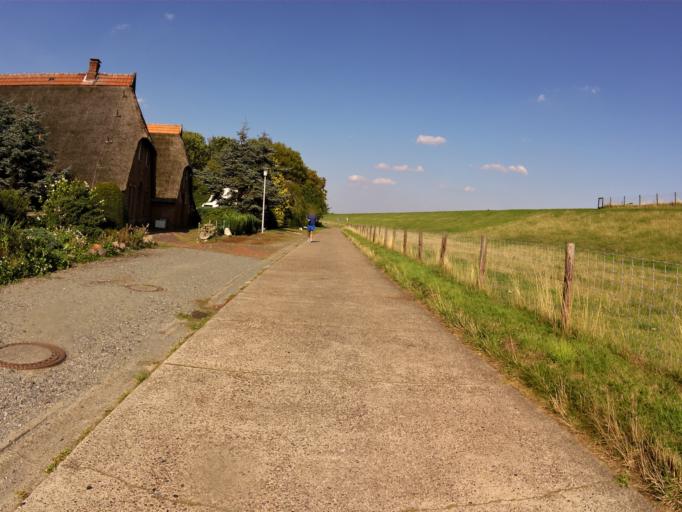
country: DE
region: Lower Saxony
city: Brake (Unterweser)
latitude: 53.3974
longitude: 8.4615
